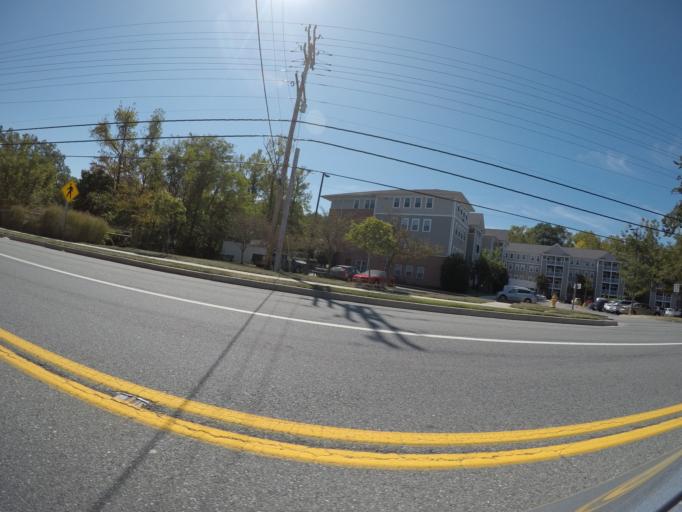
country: US
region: Maryland
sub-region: Harford County
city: Aberdeen
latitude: 39.5180
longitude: -76.1828
